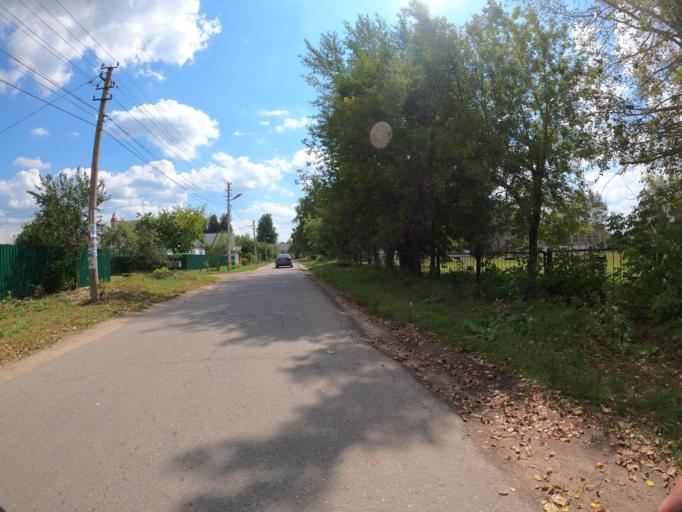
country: RU
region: Moskovskaya
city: Lopatinskiy
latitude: 55.2798
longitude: 38.7444
